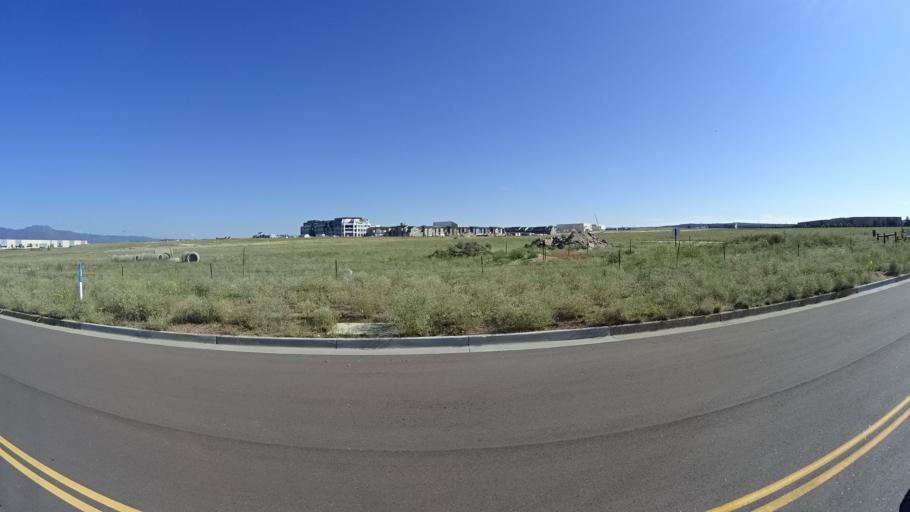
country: US
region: Colorado
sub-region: El Paso County
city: Gleneagle
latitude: 38.9825
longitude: -104.7945
